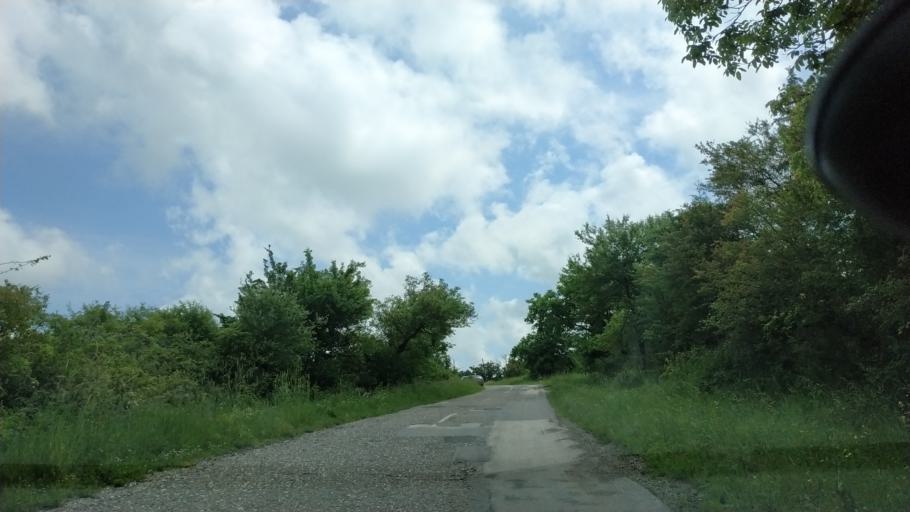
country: RS
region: Central Serbia
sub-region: Zajecarski Okrug
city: Boljevac
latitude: 43.8305
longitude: 21.9681
